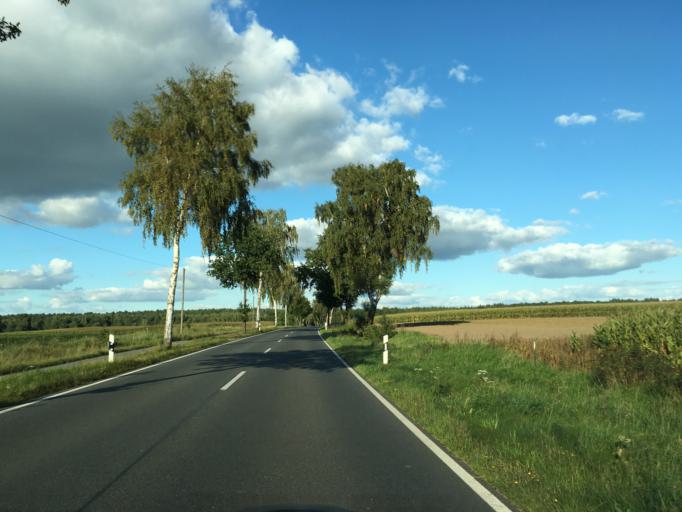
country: DE
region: Lower Saxony
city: Kirchgellersen
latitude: 53.2339
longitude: 10.3067
